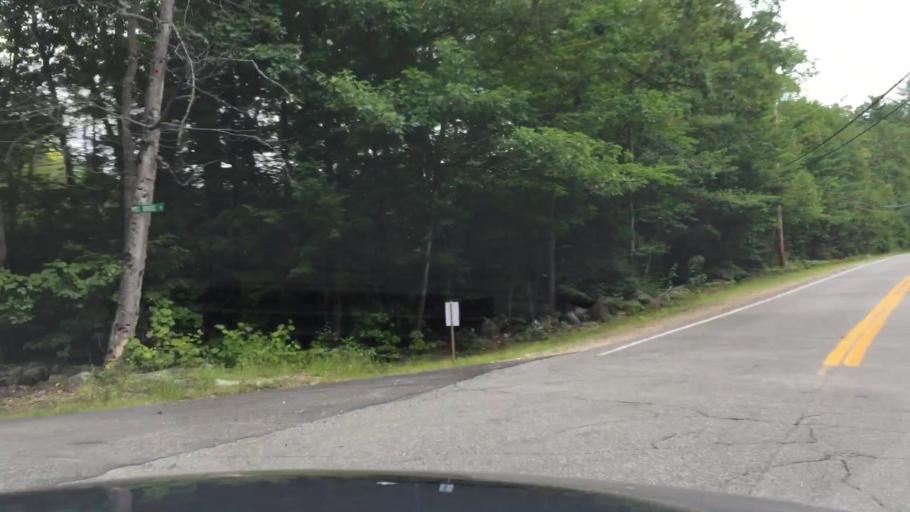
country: US
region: New Hampshire
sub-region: Carroll County
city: Sandwich
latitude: 43.7847
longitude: -71.4695
